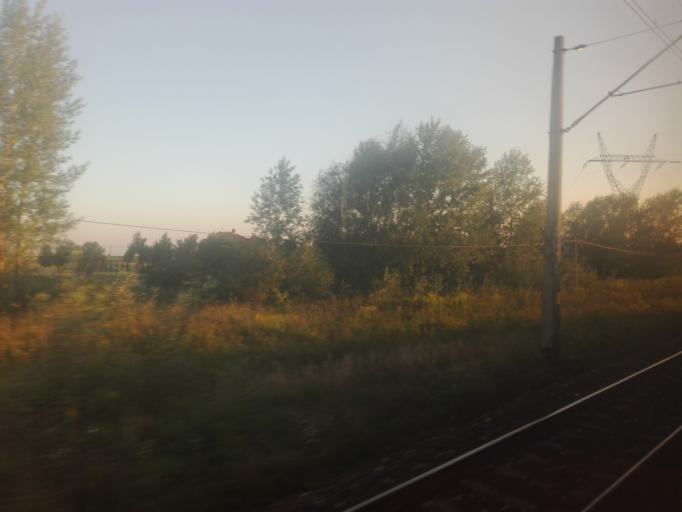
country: PL
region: Masovian Voivodeship
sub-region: Powiat warszawski zachodni
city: Bieniewice
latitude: 52.1862
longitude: 20.5825
